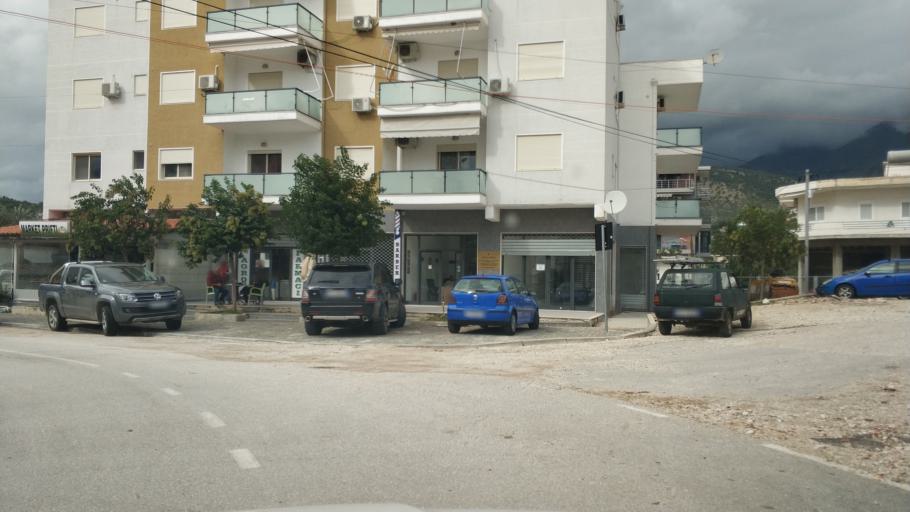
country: AL
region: Vlore
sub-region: Rrethi i Vlores
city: Himare
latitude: 40.1028
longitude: 19.7459
